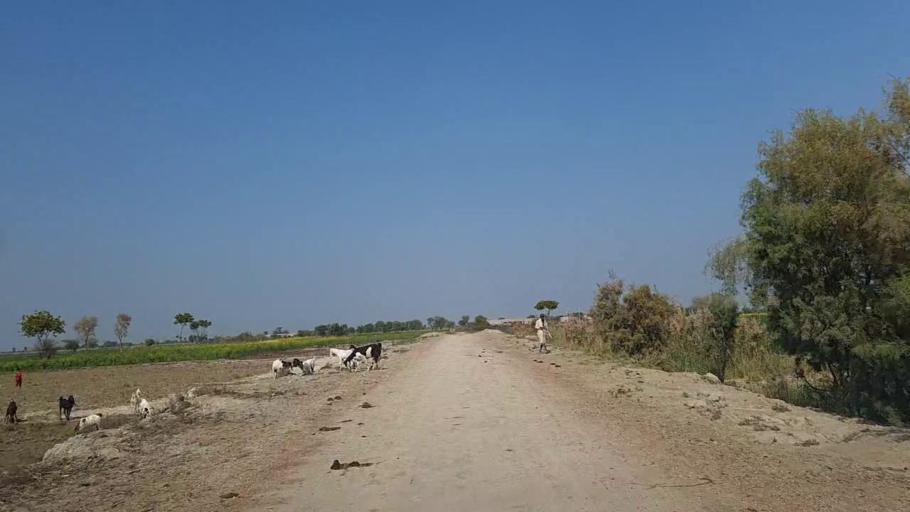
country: PK
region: Sindh
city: Nawabshah
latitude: 26.2922
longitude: 68.5138
